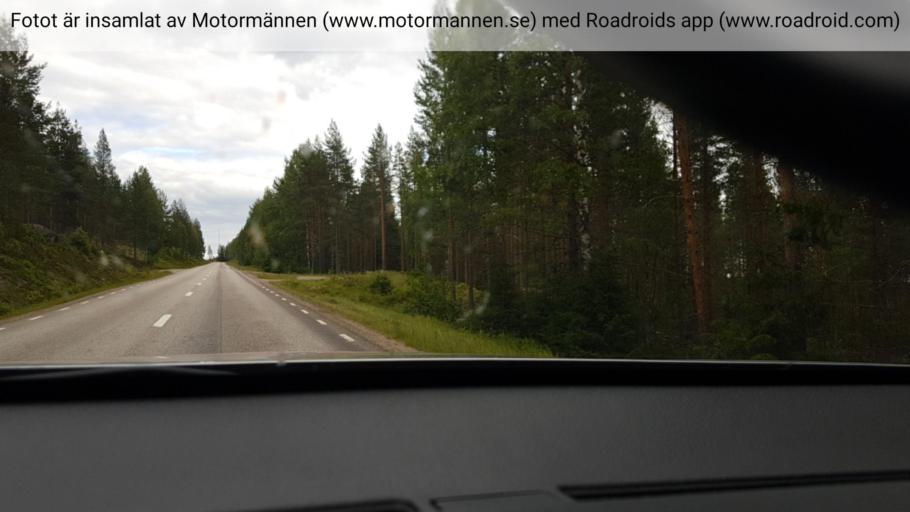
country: NO
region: Hedmark
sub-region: Trysil
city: Innbygda
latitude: 61.0292
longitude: 12.4822
